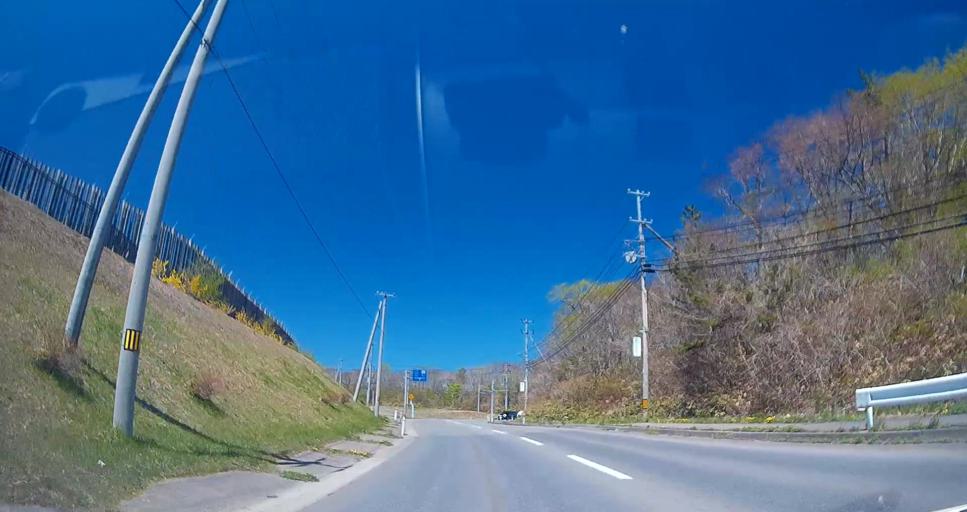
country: JP
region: Aomori
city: Misawa
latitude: 40.9800
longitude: 141.3588
